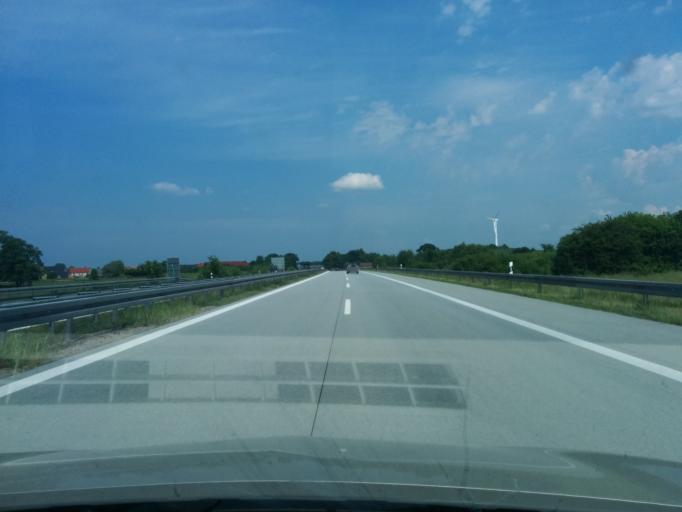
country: DE
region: Brandenburg
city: Althuttendorf
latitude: 52.9577
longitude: 13.8104
